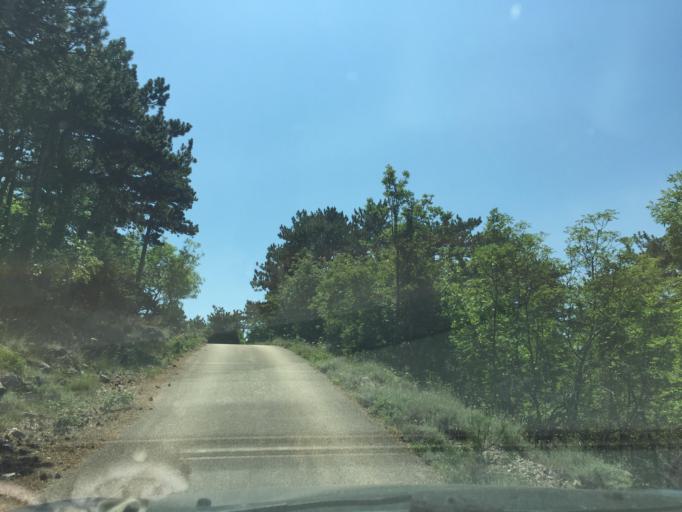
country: HR
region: Primorsko-Goranska
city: Punat
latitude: 45.0160
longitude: 14.6770
